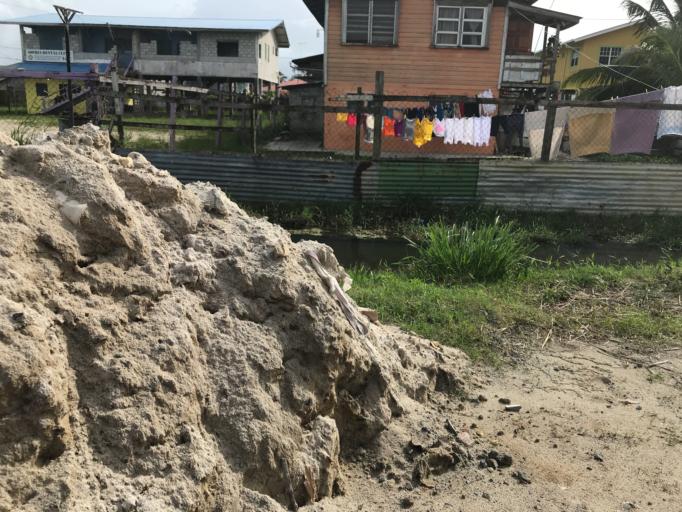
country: GY
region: Demerara-Mahaica
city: Georgetown
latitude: 6.7969
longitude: -58.1266
